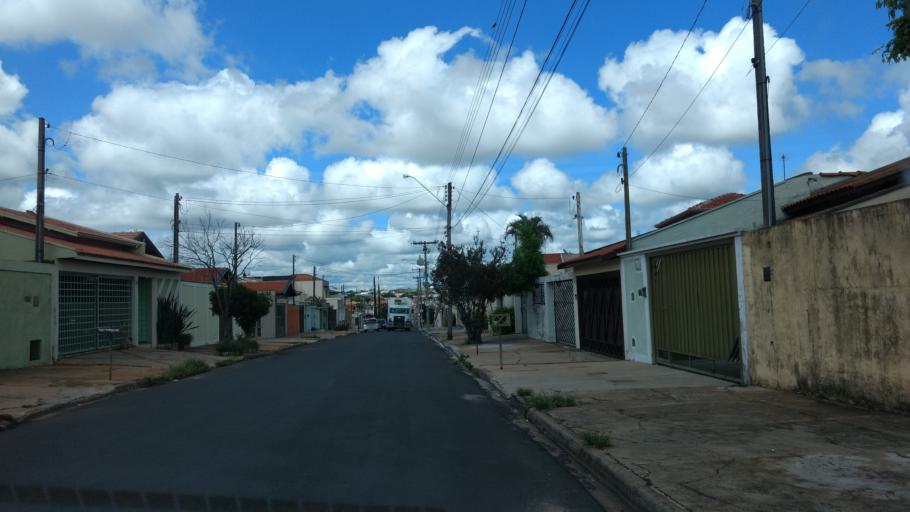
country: BR
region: Sao Paulo
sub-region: Botucatu
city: Botucatu
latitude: -22.8596
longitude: -48.4497
